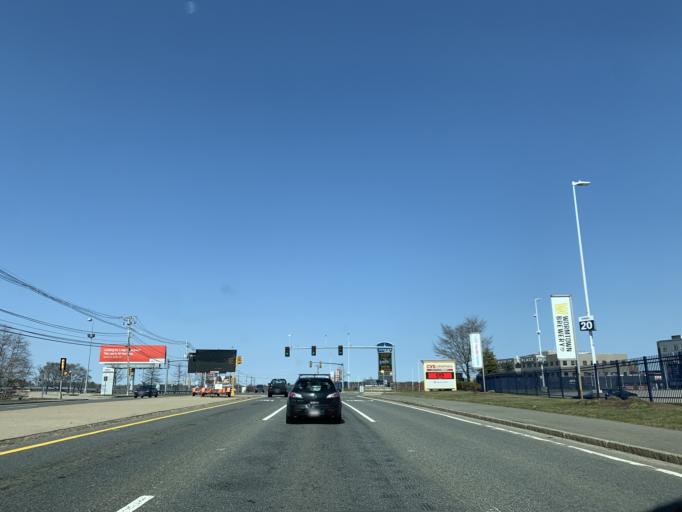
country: US
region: Massachusetts
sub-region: Norfolk County
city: Foxborough
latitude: 42.0906
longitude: -71.2708
